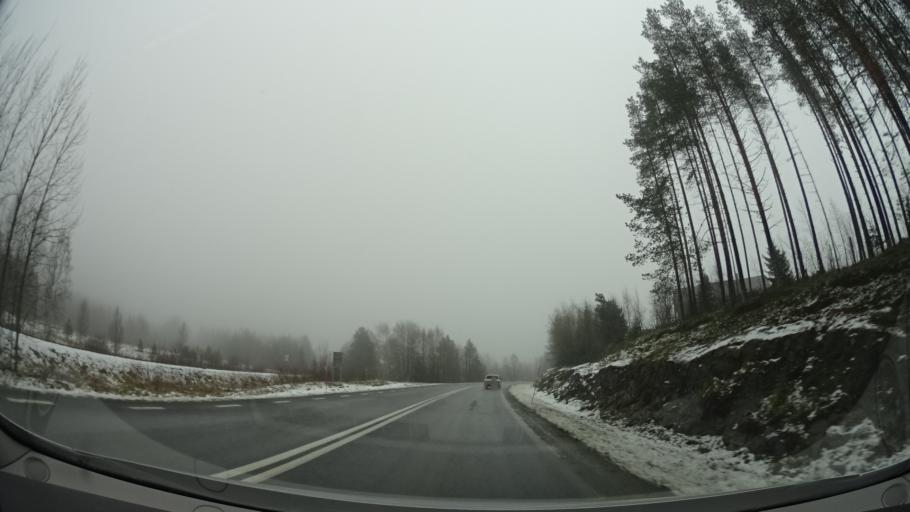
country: SE
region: Vaesterbotten
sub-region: Dorotea Kommun
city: Dorotea
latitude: 64.2555
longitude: 16.4477
